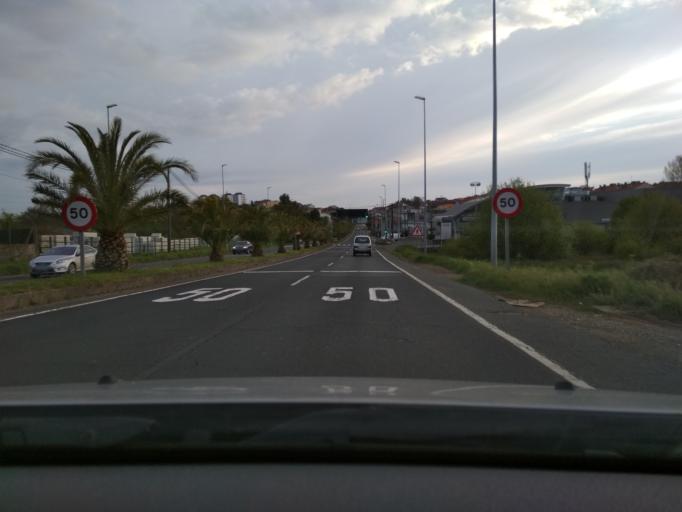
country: ES
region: Galicia
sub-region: Provincia da Coruna
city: Santiago de Compostela
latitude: 42.9021
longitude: -8.5215
